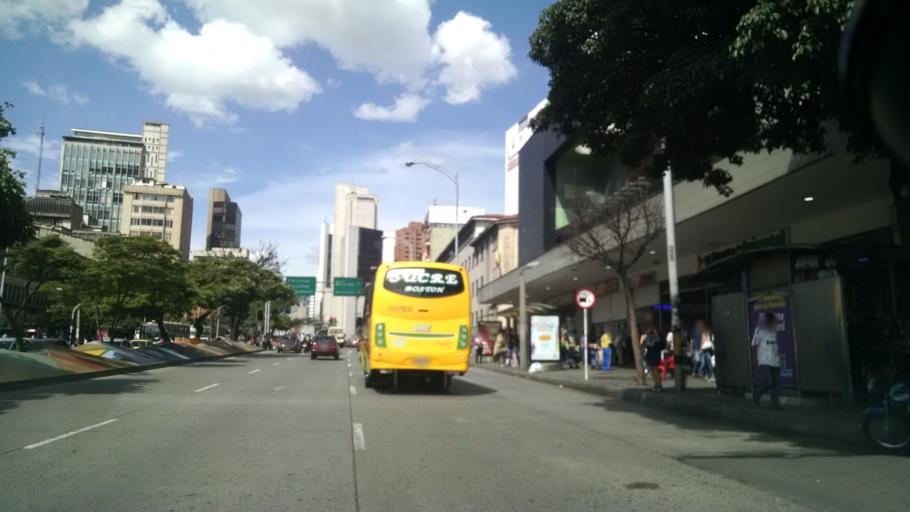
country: CO
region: Antioquia
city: Medellin
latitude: 6.2464
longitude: -75.5666
